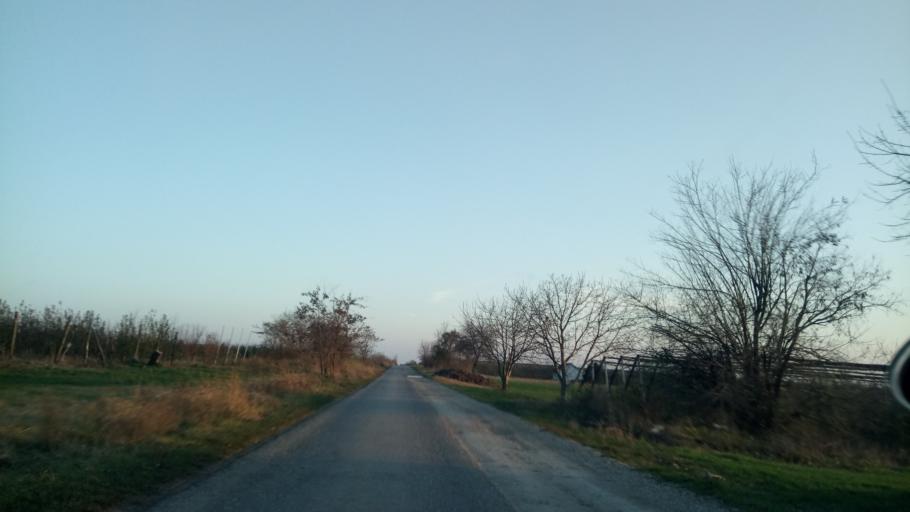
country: RS
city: Novi Slankamen
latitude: 45.1192
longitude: 20.2683
